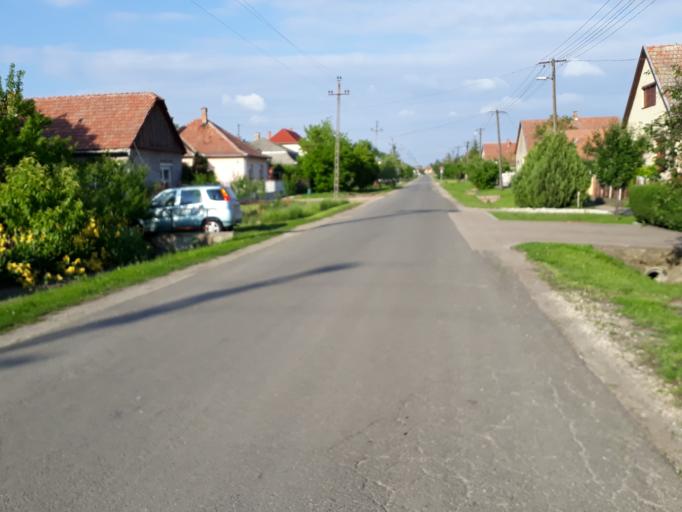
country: HU
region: Jasz-Nagykun-Szolnok
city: Ujszasz
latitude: 47.3118
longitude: 20.0933
